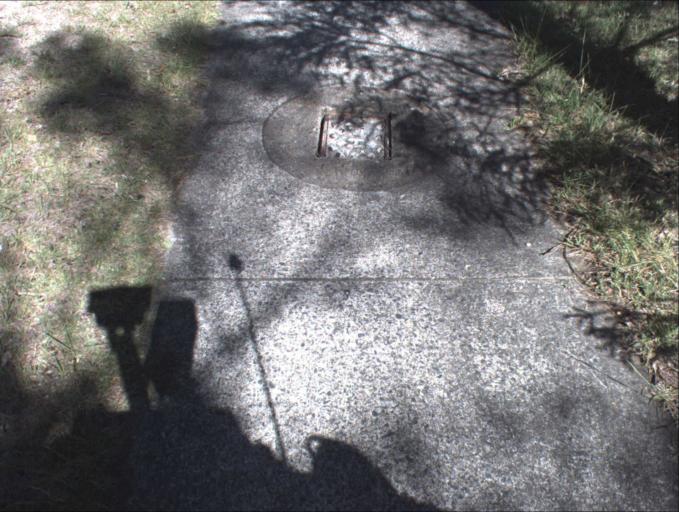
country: AU
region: Queensland
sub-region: Logan
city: Springwood
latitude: -27.6241
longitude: 153.1339
